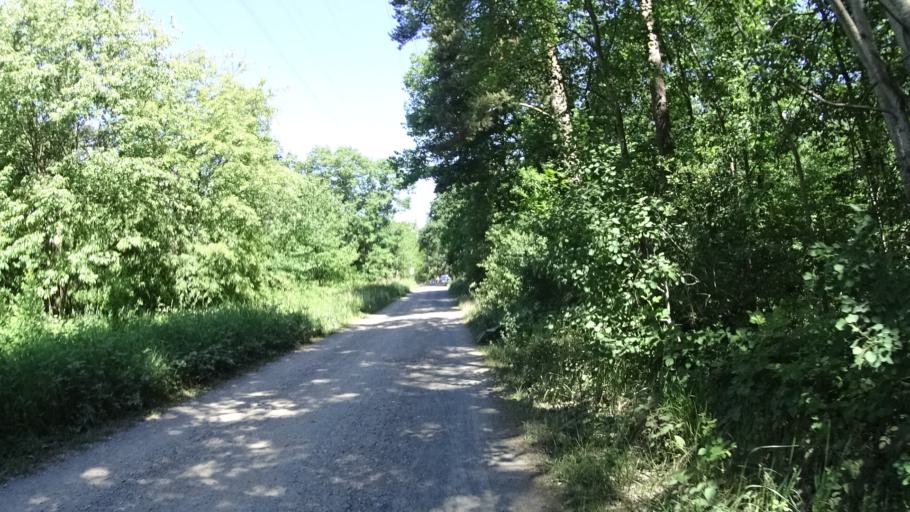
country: DE
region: Hesse
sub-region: Regierungsbezirk Darmstadt
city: Buttelborn
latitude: 49.9036
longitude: 8.5509
